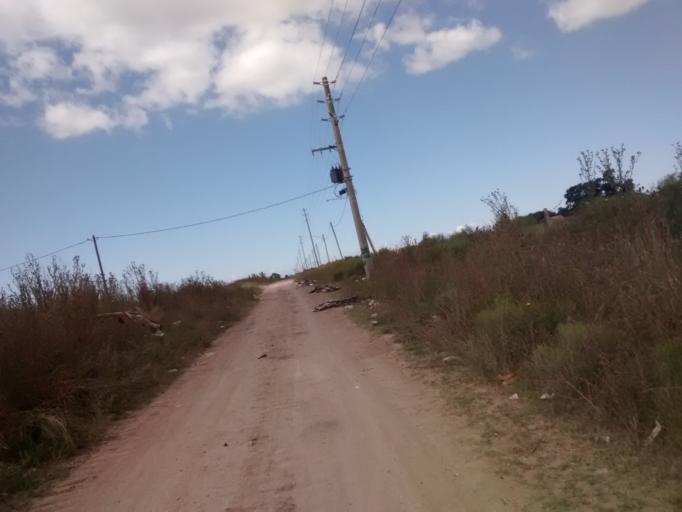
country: AR
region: Buenos Aires
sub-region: Partido de La Plata
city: La Plata
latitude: -34.9705
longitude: -57.9387
